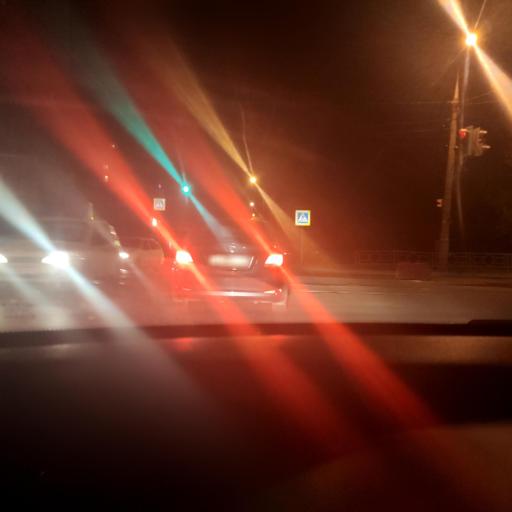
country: RU
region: Samara
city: Samara
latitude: 53.2314
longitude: 50.2249
